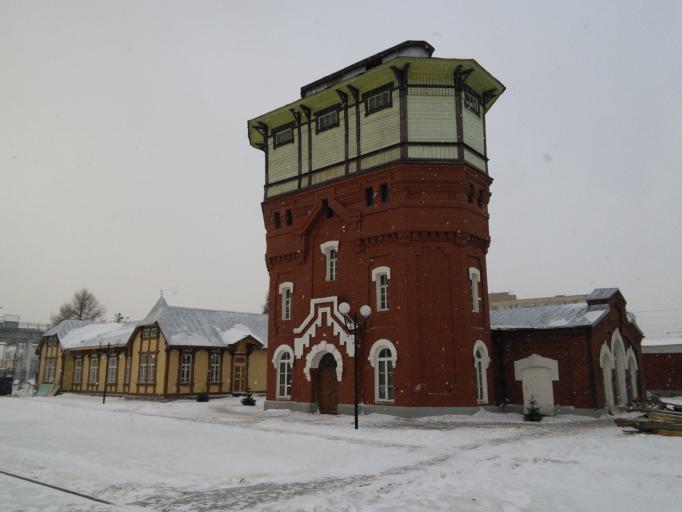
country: RU
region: Moskovskaya
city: Koptevo
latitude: 55.8139
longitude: 37.5286
